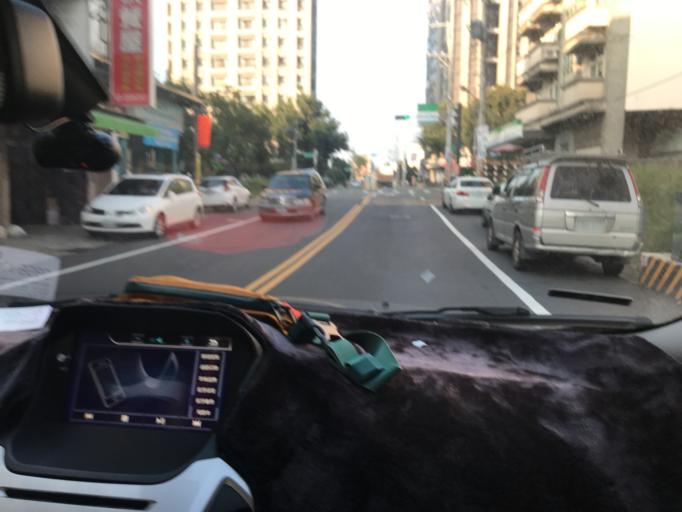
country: TW
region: Taiwan
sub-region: Hsinchu
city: Zhubei
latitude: 24.8222
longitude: 121.0327
